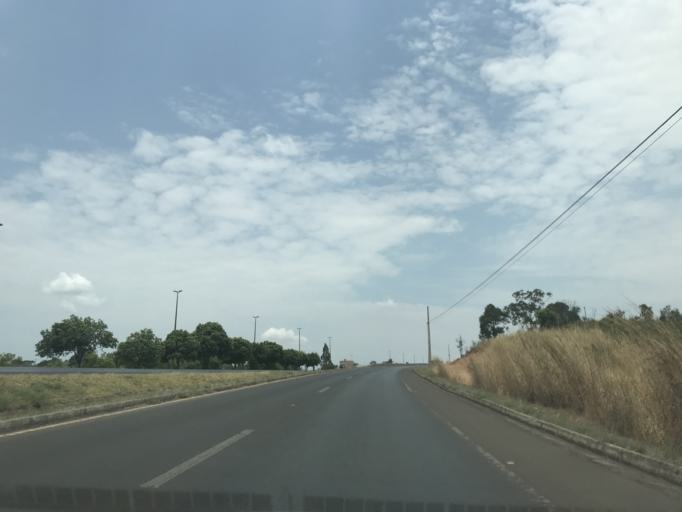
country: BR
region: Federal District
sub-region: Brasilia
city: Brasilia
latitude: -15.6778
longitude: -47.8275
